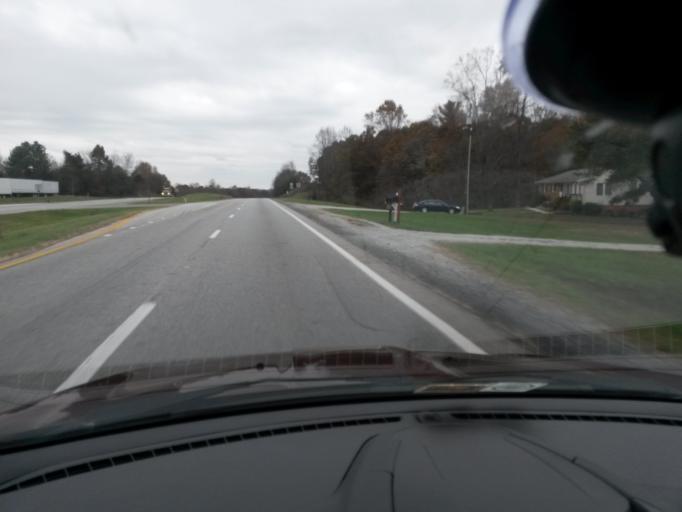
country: US
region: Virginia
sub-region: Nelson County
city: Lovingston
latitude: 37.6718
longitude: -78.9534
